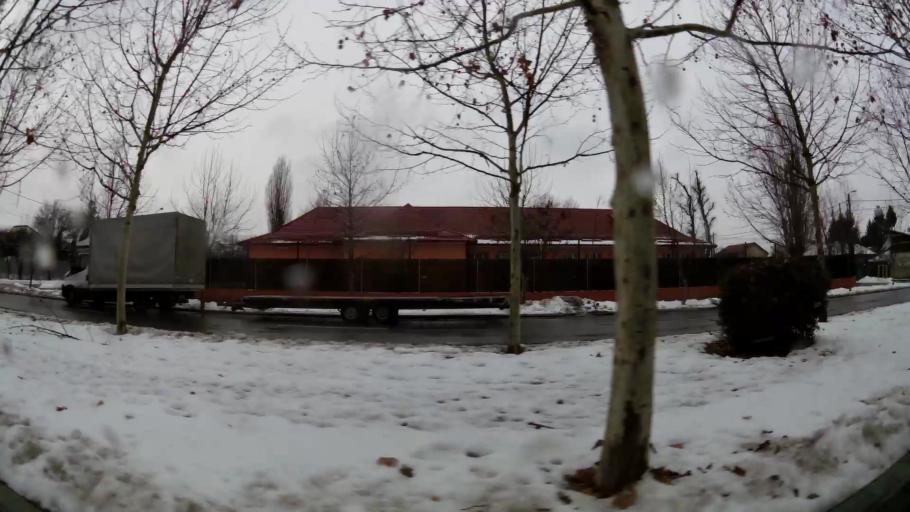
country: RO
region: Ilfov
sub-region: Comuna Chiajna
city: Rosu
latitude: 44.4880
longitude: 26.0218
